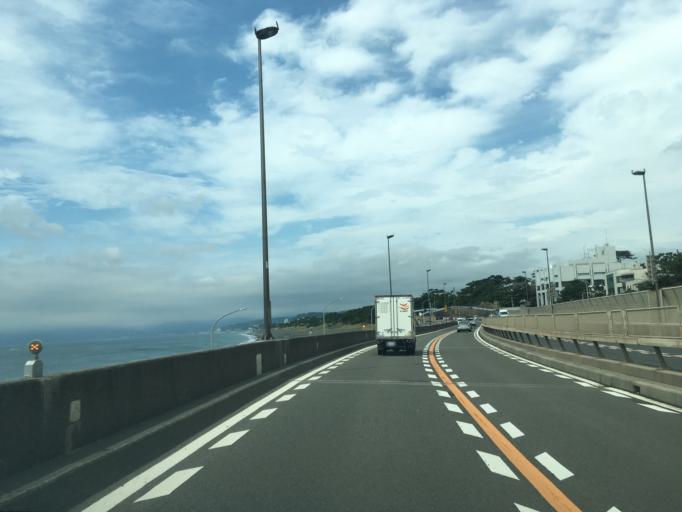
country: JP
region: Kanagawa
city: Oiso
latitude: 35.3059
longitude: 139.3138
